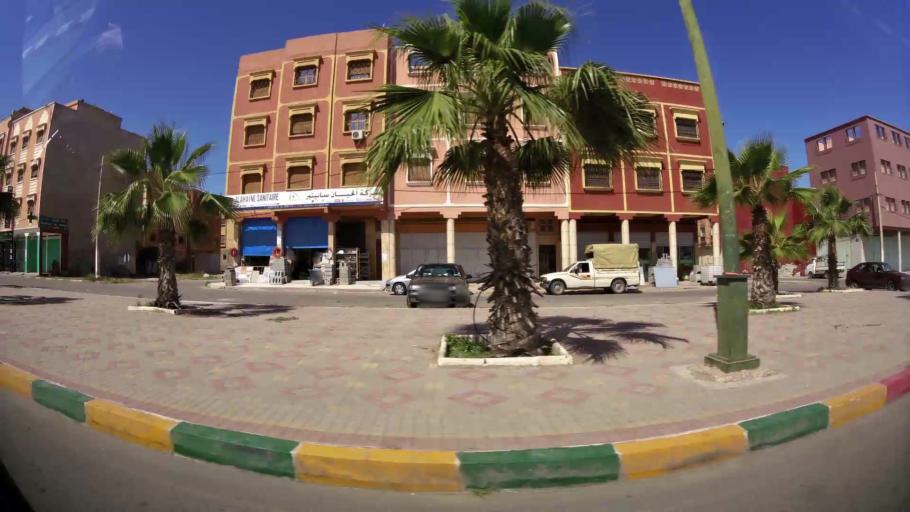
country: MA
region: Souss-Massa-Draa
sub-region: Inezgane-Ait Mellou
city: Inezgane
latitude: 30.3292
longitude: -9.5039
